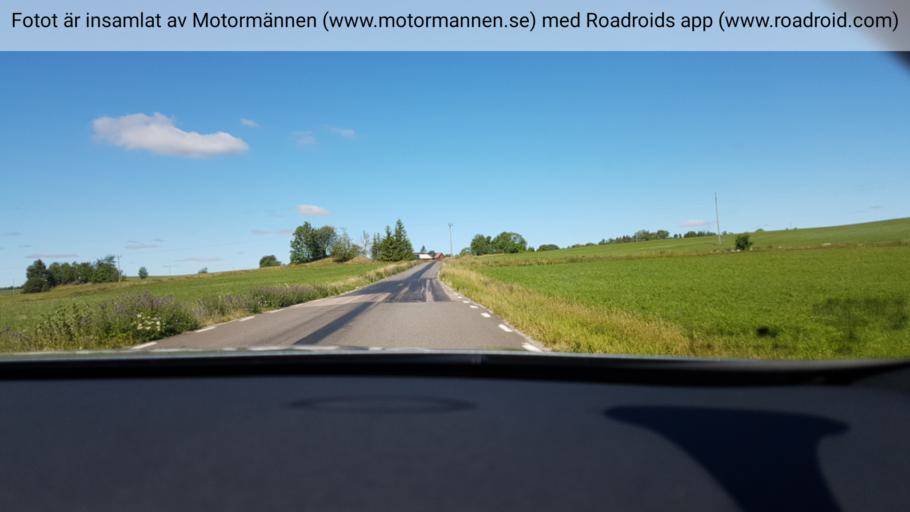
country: SE
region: Vaestra Goetaland
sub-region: Falkopings Kommun
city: Akarp
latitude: 58.2548
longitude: 13.6801
